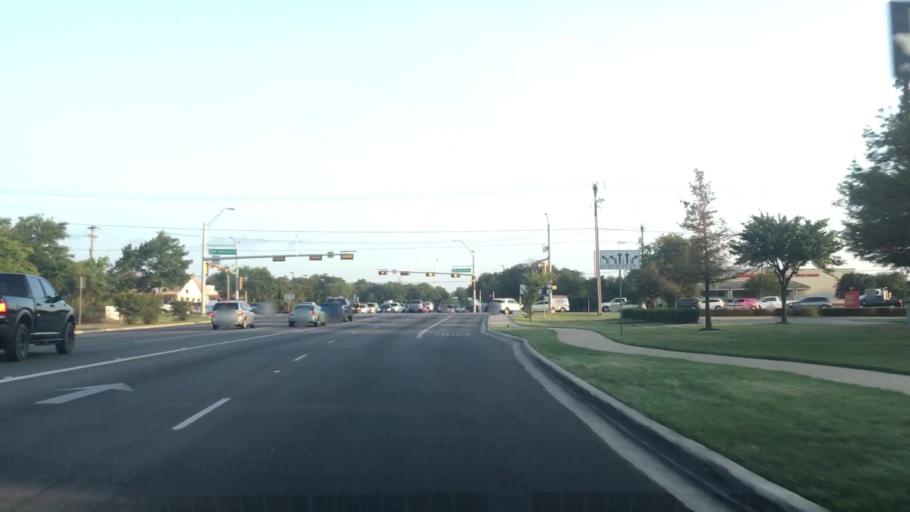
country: US
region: Texas
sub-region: Williamson County
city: Cedar Park
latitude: 30.5136
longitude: -97.8506
